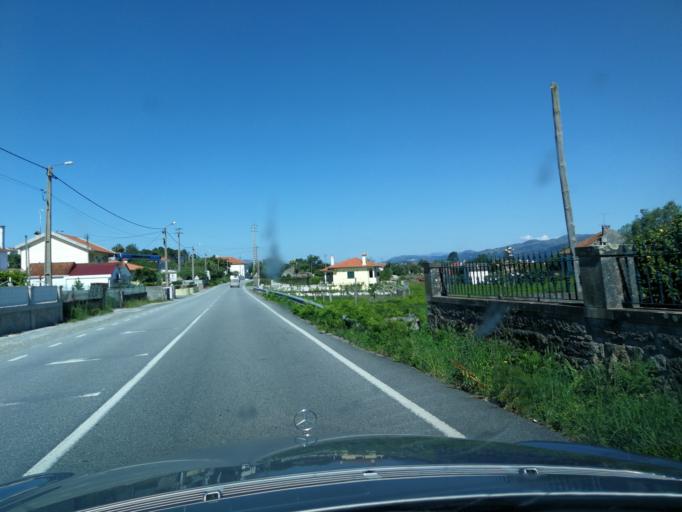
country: PT
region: Viana do Castelo
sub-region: Viana do Castelo
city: Darque
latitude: 41.7130
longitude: -8.7399
